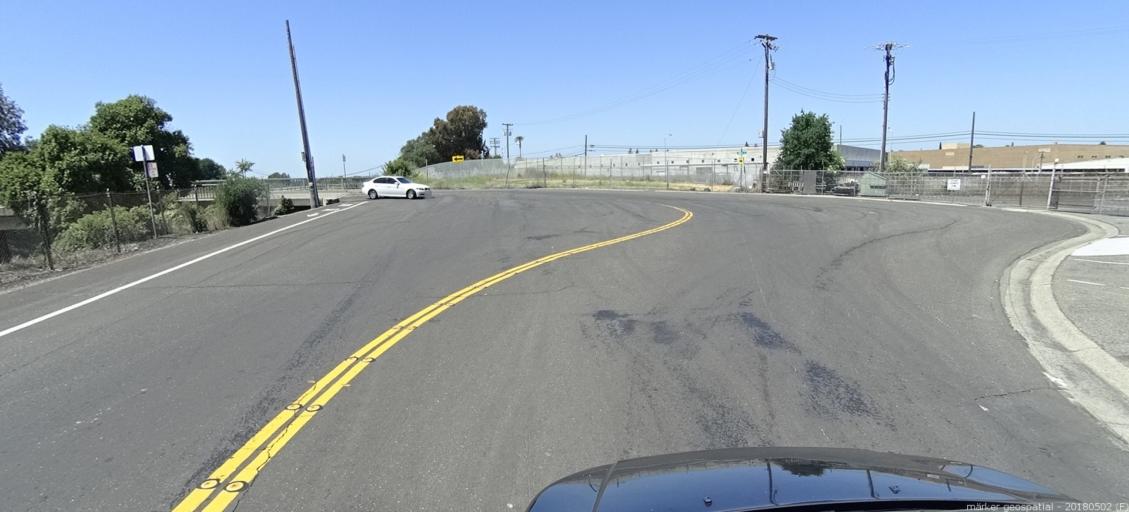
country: US
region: California
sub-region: Sacramento County
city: Sacramento
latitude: 38.6004
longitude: -121.4456
